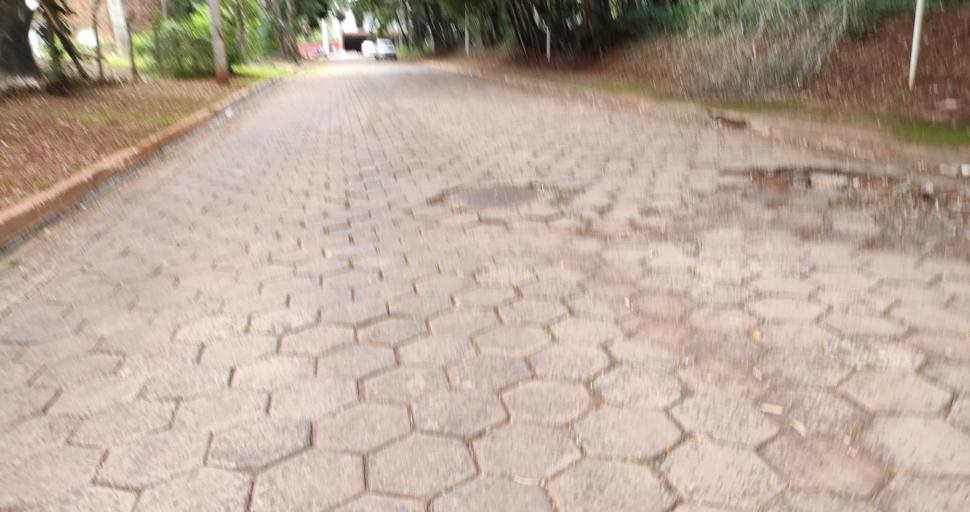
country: AR
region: Misiones
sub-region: Departamento de Iguazu
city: Puerto Iguazu
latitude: -25.5945
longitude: -54.5763
